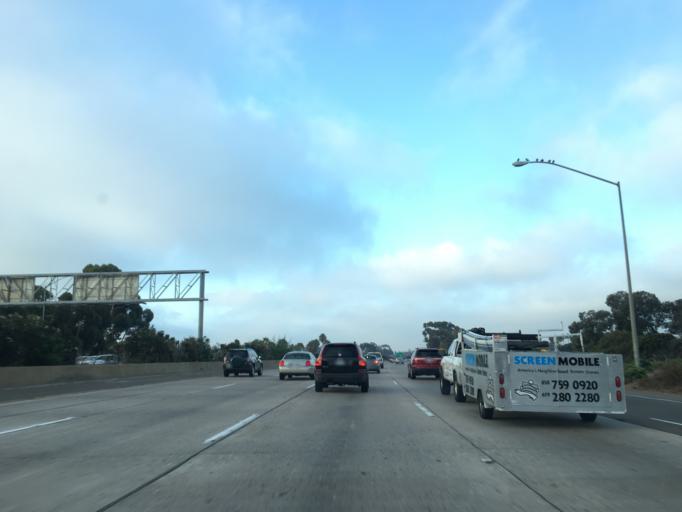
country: US
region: California
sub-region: San Diego County
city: San Diego
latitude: 32.7885
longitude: -117.2072
